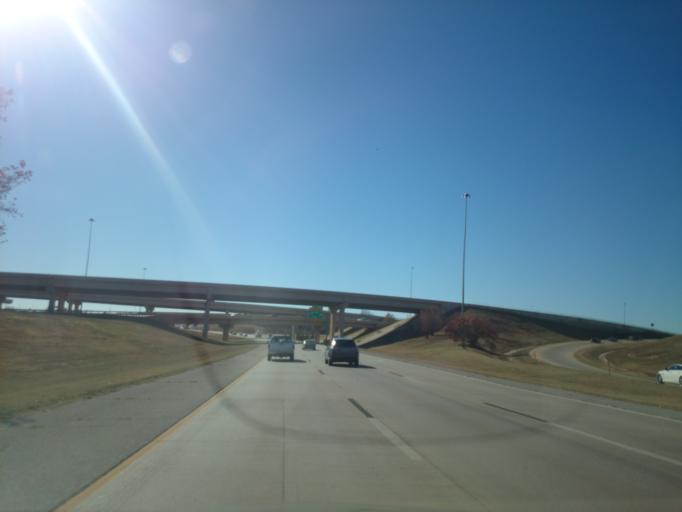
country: US
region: Oklahoma
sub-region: Oklahoma County
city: Edmond
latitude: 35.6026
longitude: -97.4294
